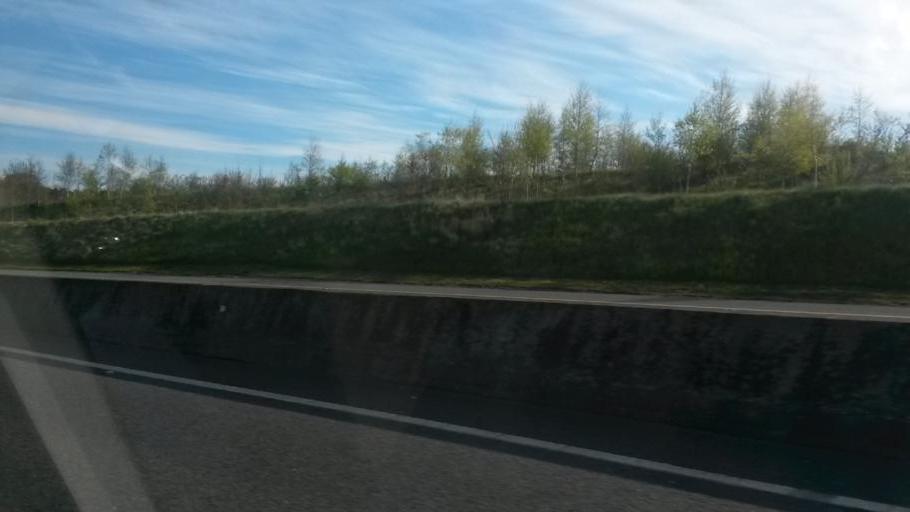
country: IE
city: Kentstown
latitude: 53.5886
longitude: -6.5817
